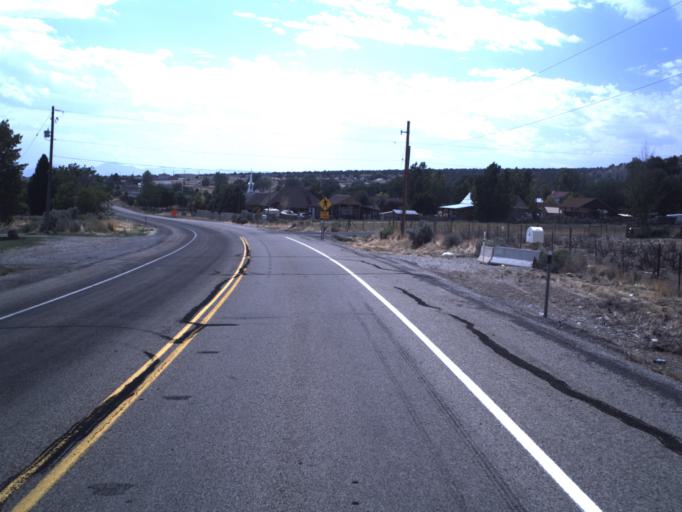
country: US
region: Utah
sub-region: Utah County
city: Eagle Mountain
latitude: 40.3314
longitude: -112.1020
